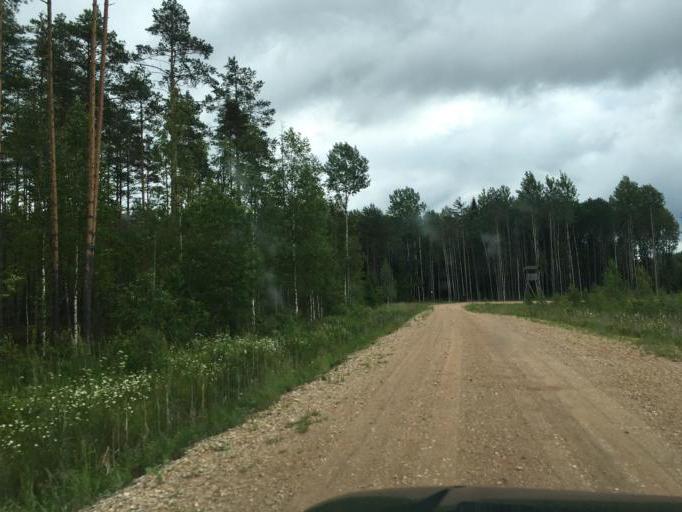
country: LV
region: Vilaka
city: Vilaka
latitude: 57.3882
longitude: 27.4941
